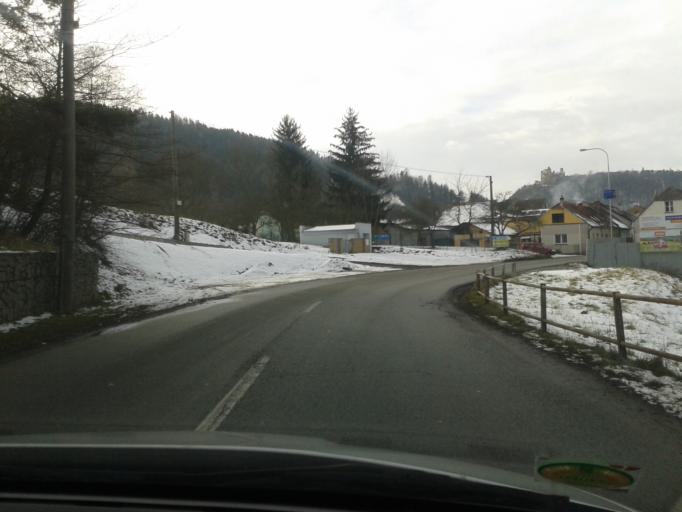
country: CZ
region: South Moravian
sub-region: Okres Blansko
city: Boskovice
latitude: 49.4826
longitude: 16.6785
